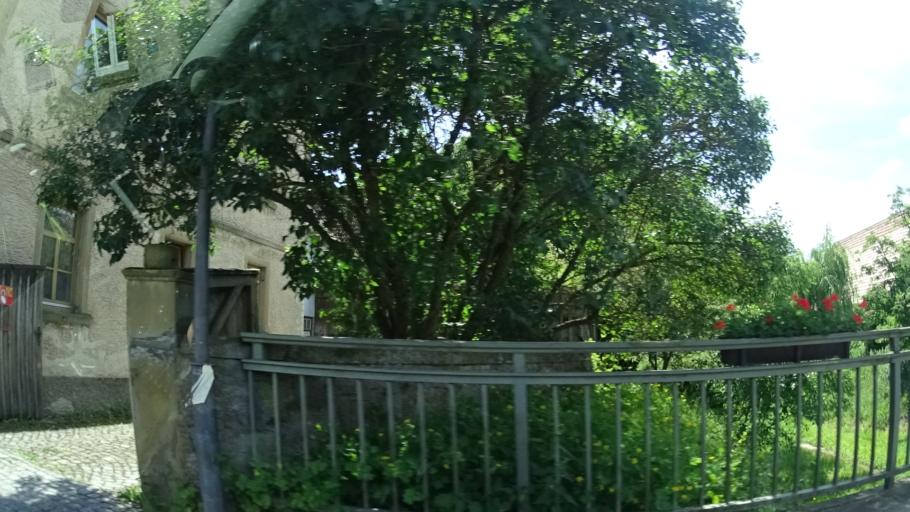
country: DE
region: Bavaria
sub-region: Regierungsbezirk Unterfranken
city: Arnstein
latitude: 50.0188
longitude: 10.0057
